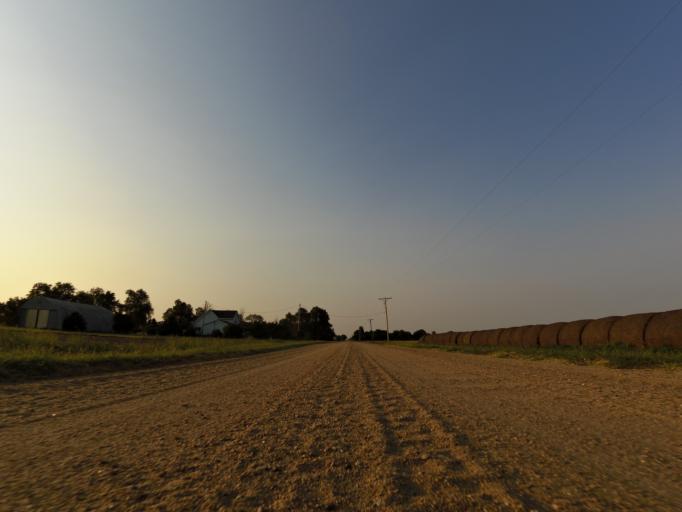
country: US
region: Kansas
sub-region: Reno County
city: South Hutchinson
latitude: 38.0045
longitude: -97.9955
